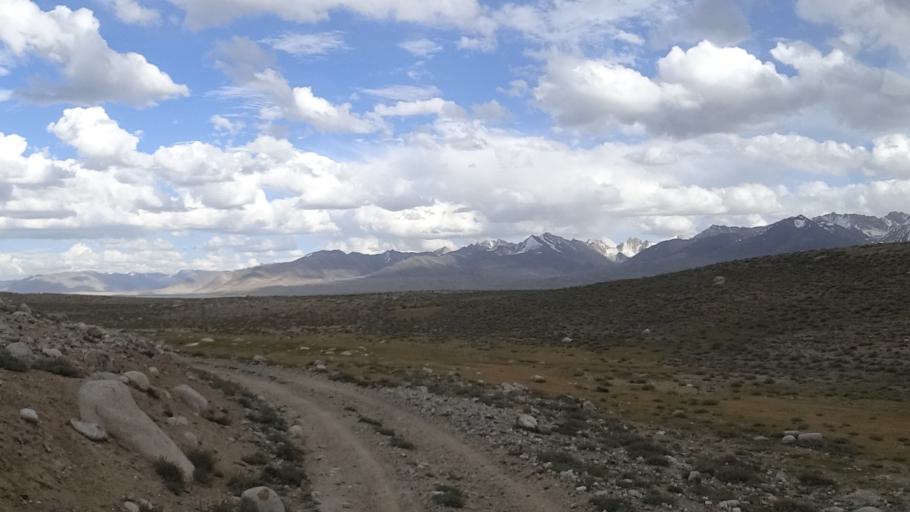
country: TJ
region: Gorno-Badakhshan
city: Murghob
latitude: 37.4689
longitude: 73.6012
